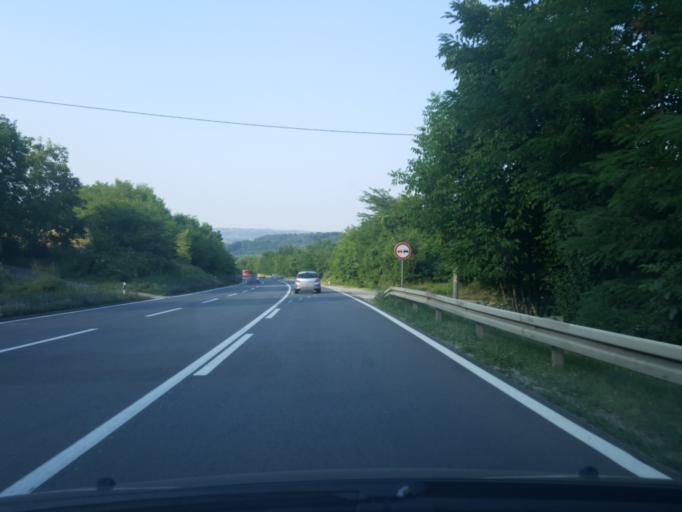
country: RS
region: Central Serbia
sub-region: Belgrade
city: Sopot
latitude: 44.5492
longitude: 20.6630
